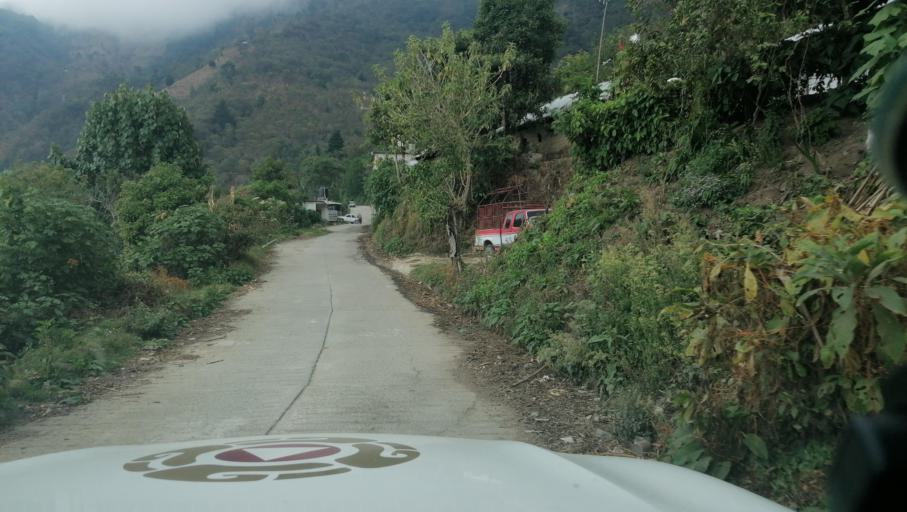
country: GT
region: San Marcos
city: Tacana
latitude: 15.2024
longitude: -92.1809
